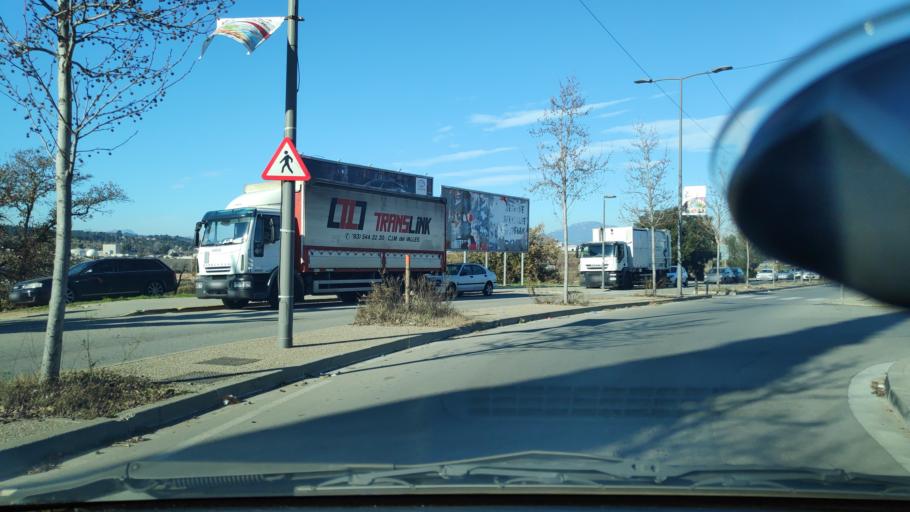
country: ES
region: Catalonia
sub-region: Provincia de Barcelona
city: Barbera del Valles
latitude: 41.5125
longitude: 2.1134
